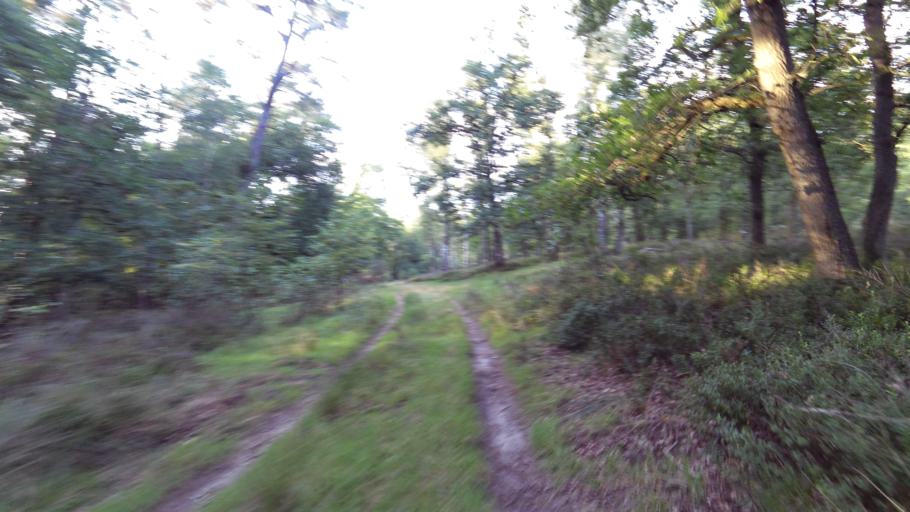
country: NL
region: Gelderland
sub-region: Gemeente Epe
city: Vaassen
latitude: 52.2939
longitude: 5.8749
